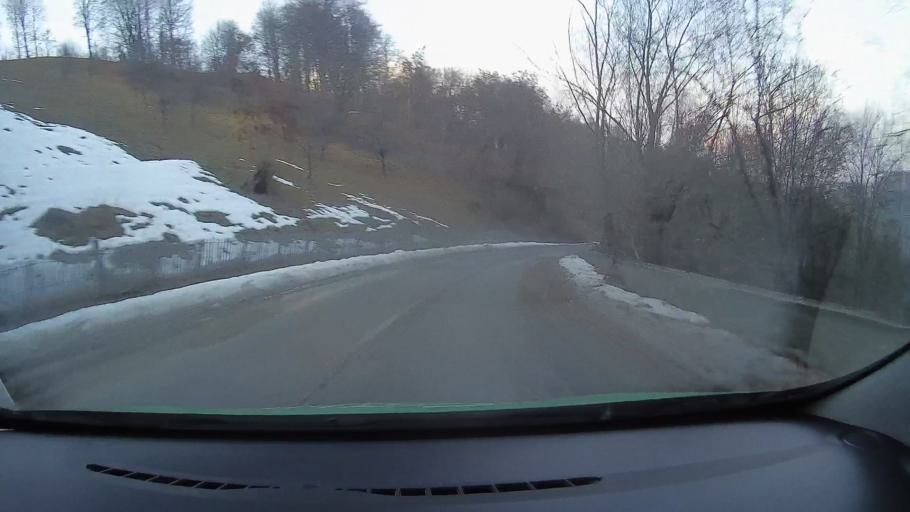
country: RO
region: Prahova
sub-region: Comuna Secaria
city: Secaria
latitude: 45.2675
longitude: 25.6750
